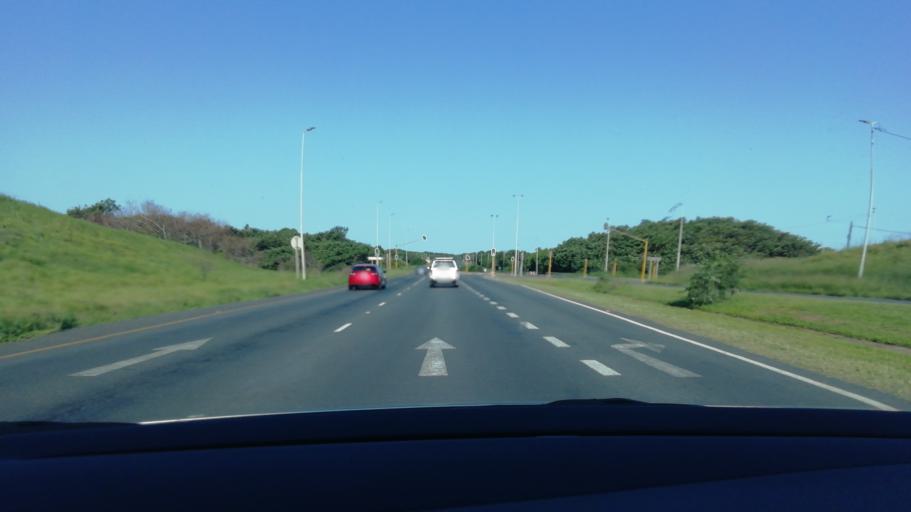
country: ZA
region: KwaZulu-Natal
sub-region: uThungulu District Municipality
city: Richards Bay
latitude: -28.7693
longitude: 32.0416
